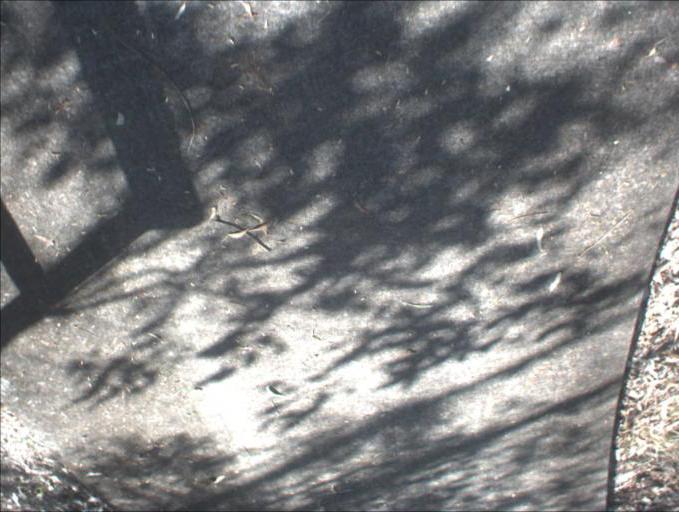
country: AU
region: Queensland
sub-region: Logan
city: Windaroo
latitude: -27.7198
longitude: 153.1728
